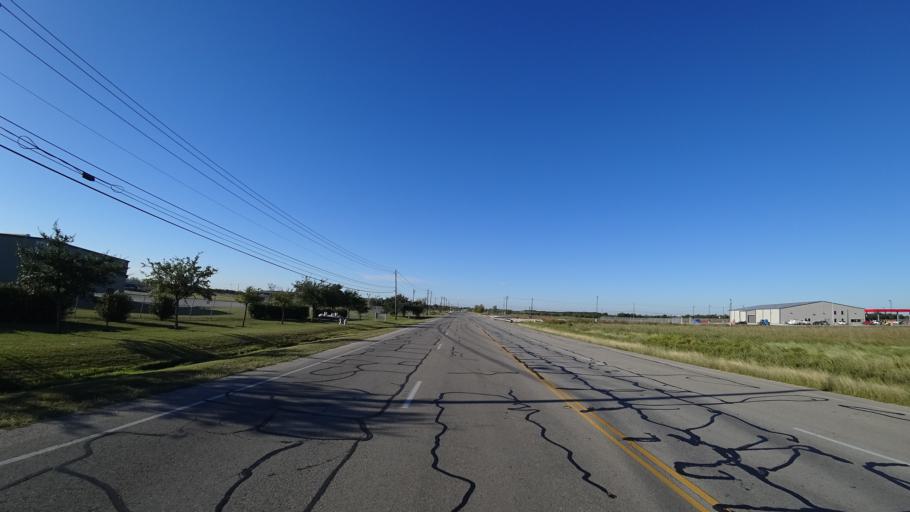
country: US
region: Texas
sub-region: Travis County
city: Manor
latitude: 30.3250
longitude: -97.6287
